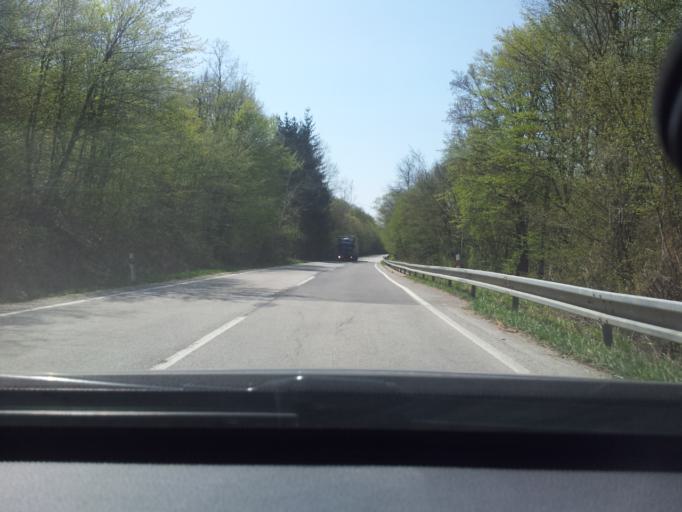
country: SK
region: Nitriansky
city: Zlate Moravce
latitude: 48.4851
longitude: 18.4191
